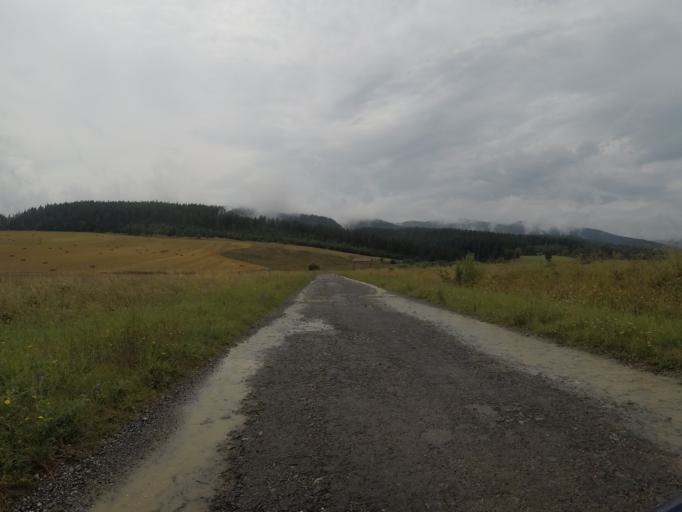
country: SK
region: Kosicky
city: Spisska Nova Ves
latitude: 48.9637
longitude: 20.4492
